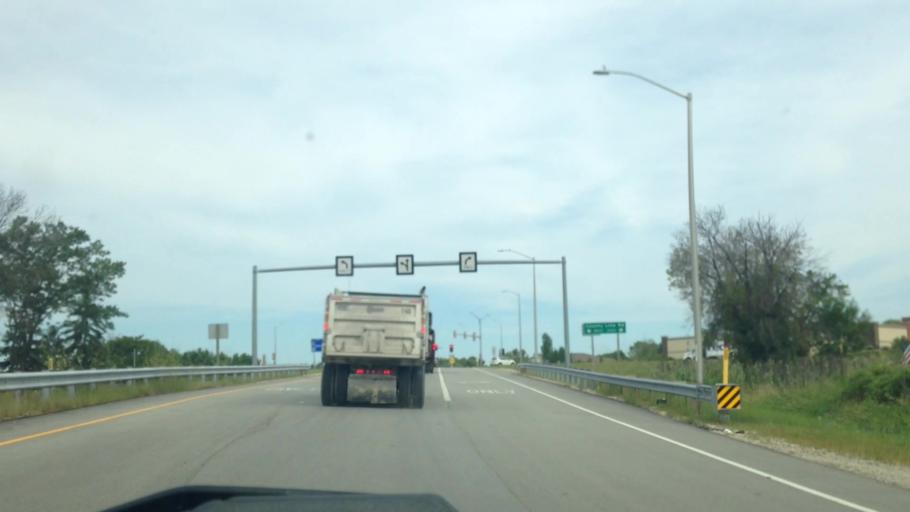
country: US
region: Wisconsin
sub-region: Waukesha County
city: Menomonee Falls
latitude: 43.1910
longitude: -88.1193
